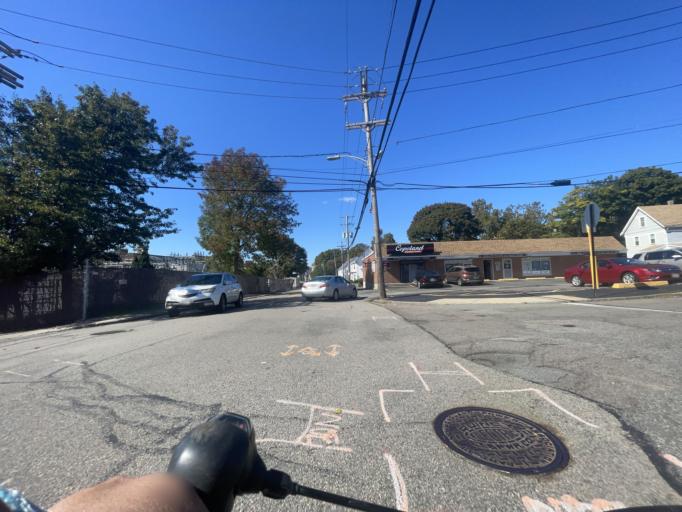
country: US
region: Massachusetts
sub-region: Norfolk County
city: Quincy
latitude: 42.2450
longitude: -71.0266
